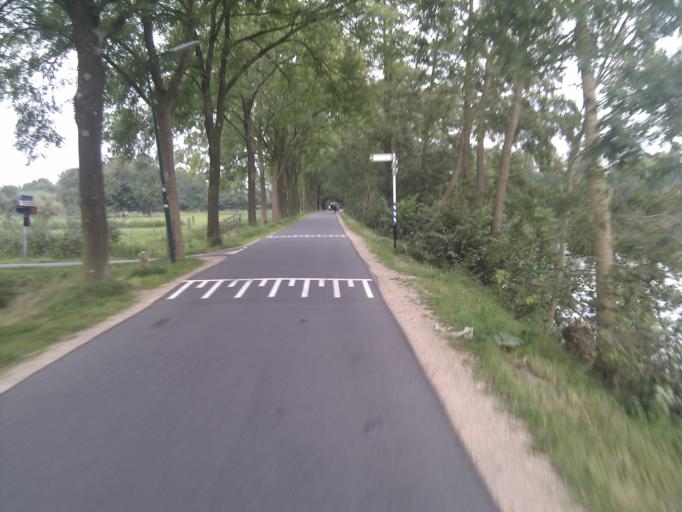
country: NL
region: Utrecht
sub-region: Gemeente De Bilt
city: De Bilt
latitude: 52.1107
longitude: 5.1583
